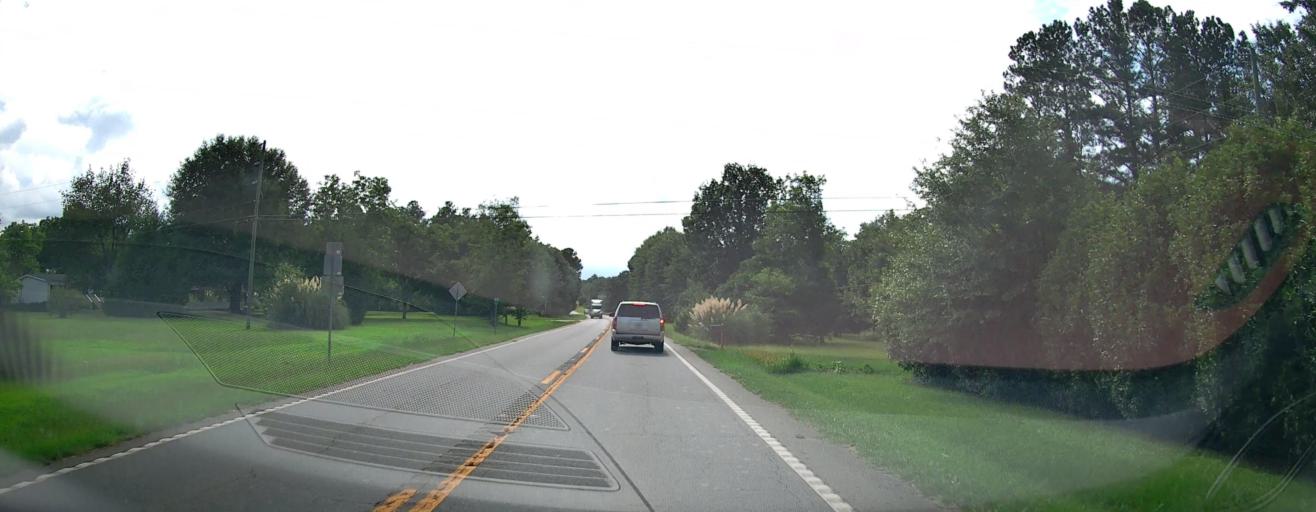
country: US
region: Georgia
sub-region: Meriwether County
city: Manchester
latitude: 32.9931
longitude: -84.5120
